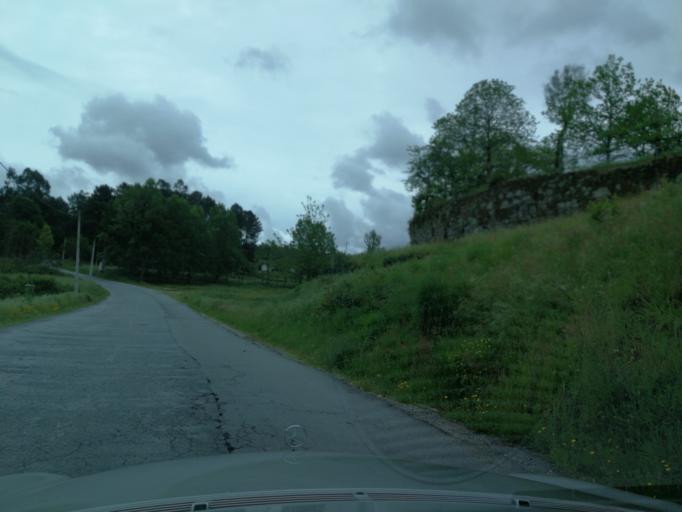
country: PT
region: Braga
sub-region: Braga
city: Adaufe
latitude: 41.6048
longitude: -8.4029
